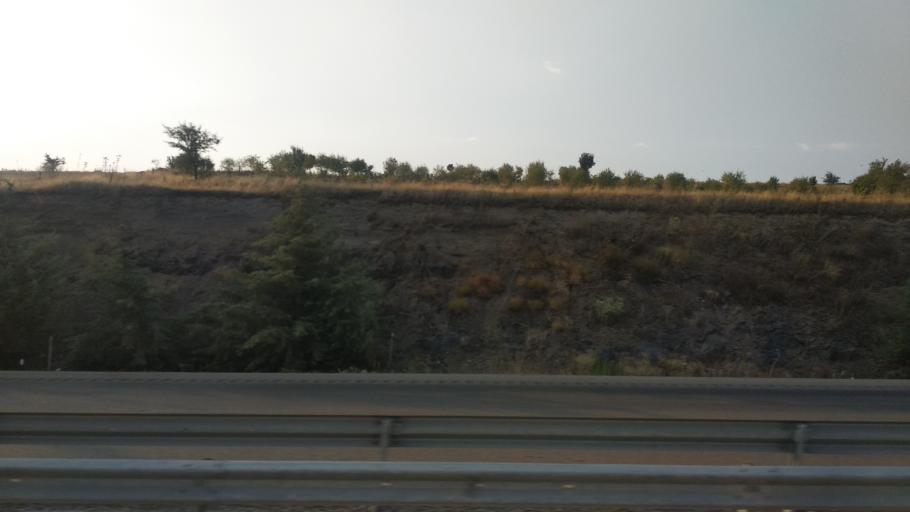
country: TR
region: Manisa
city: Menye
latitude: 38.5645
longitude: 28.5573
